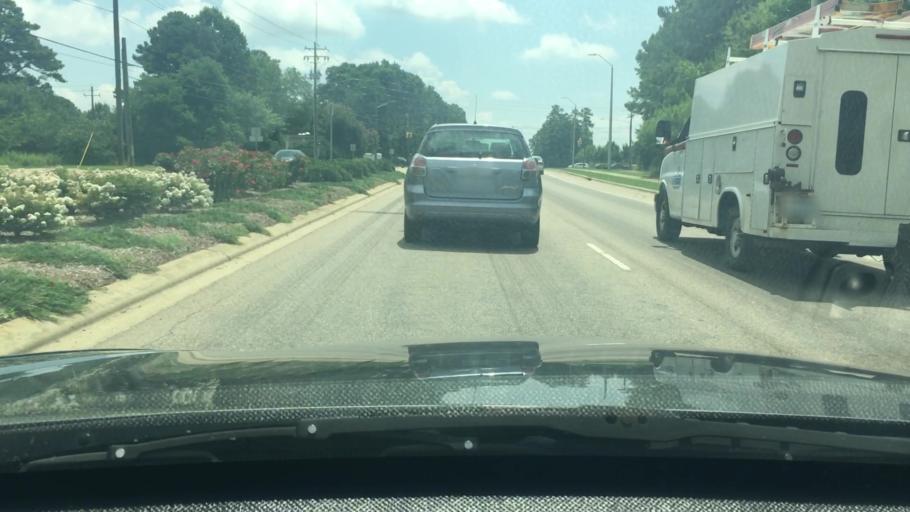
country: US
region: North Carolina
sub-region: Wake County
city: Cary
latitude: 35.7953
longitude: -78.7525
